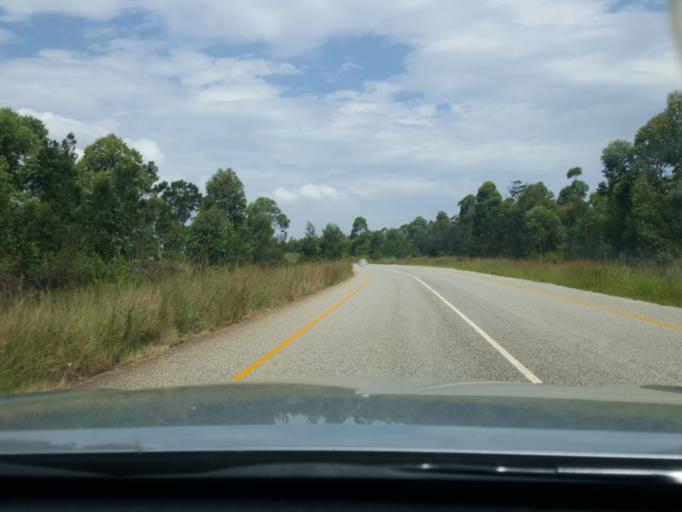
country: ZA
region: Mpumalanga
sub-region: Ehlanzeni District
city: White River
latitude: -25.1887
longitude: 30.9046
